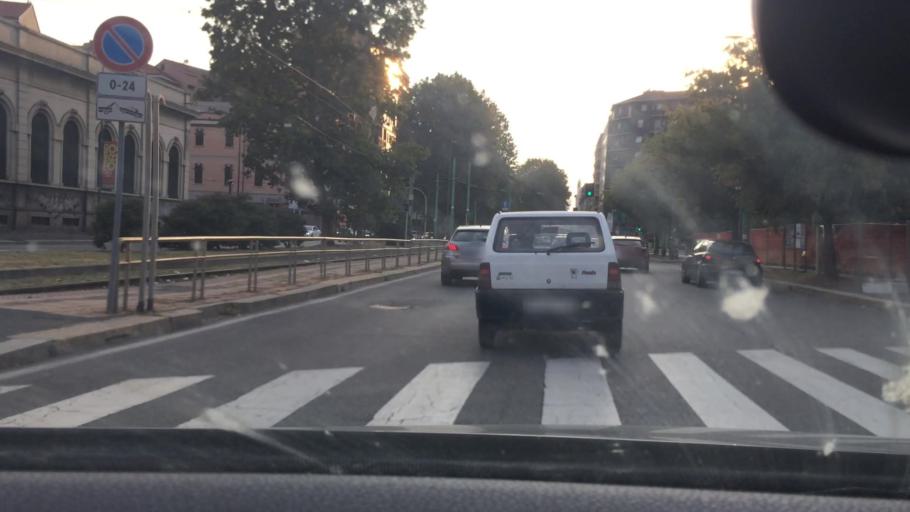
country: IT
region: Lombardy
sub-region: Citta metropolitana di Milano
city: Milano
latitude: 45.4976
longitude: 9.1863
